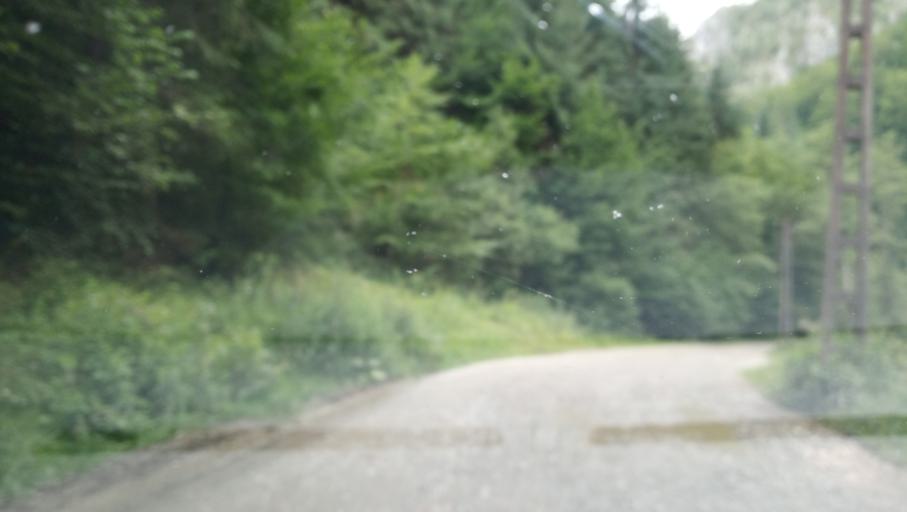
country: RO
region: Hunedoara
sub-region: Oras Petrila
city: Petrila
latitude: 45.4772
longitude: 23.4159
